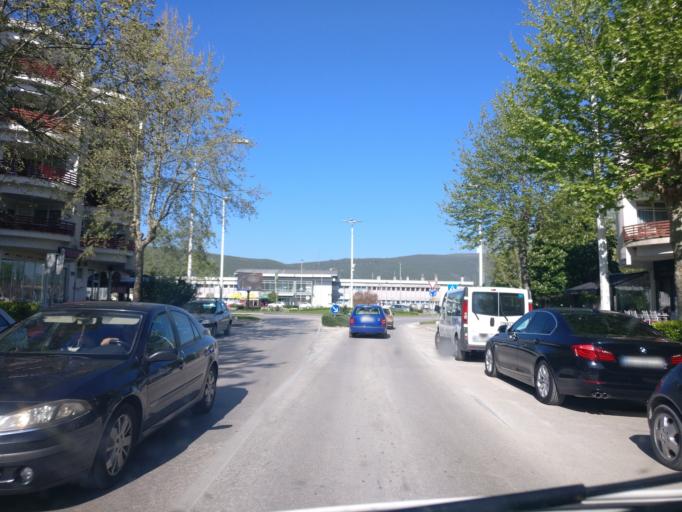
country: BA
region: Federation of Bosnia and Herzegovina
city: Capljina
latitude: 43.1098
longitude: 17.6999
